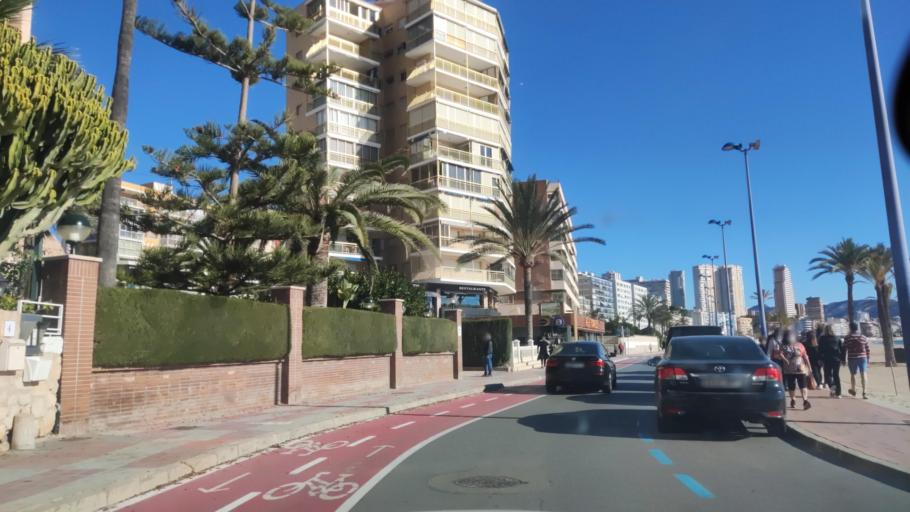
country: ES
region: Valencia
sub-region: Provincia de Alicante
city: Benidorm
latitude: 38.5352
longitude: -0.1536
